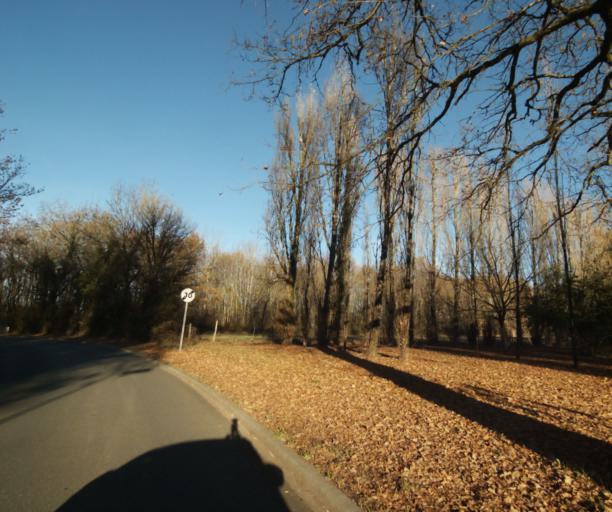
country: FR
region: Poitou-Charentes
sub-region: Departement de la Charente-Maritime
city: Fontcouverte
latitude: 45.7658
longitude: -0.6083
